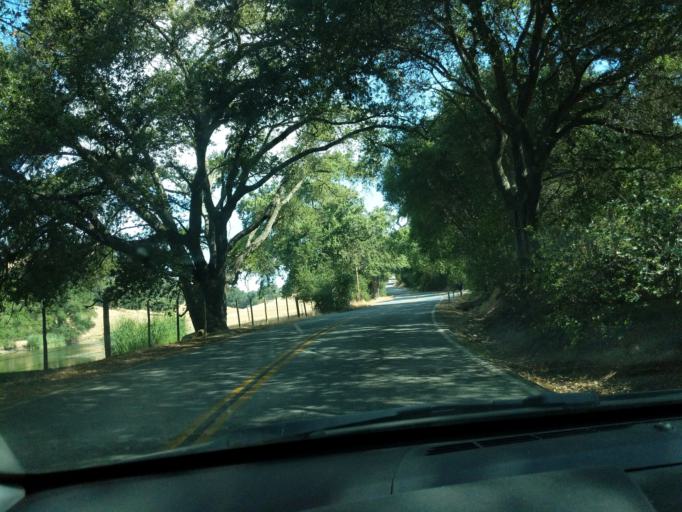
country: US
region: California
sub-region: Santa Clara County
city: Gilroy
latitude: 37.0625
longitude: -121.5216
